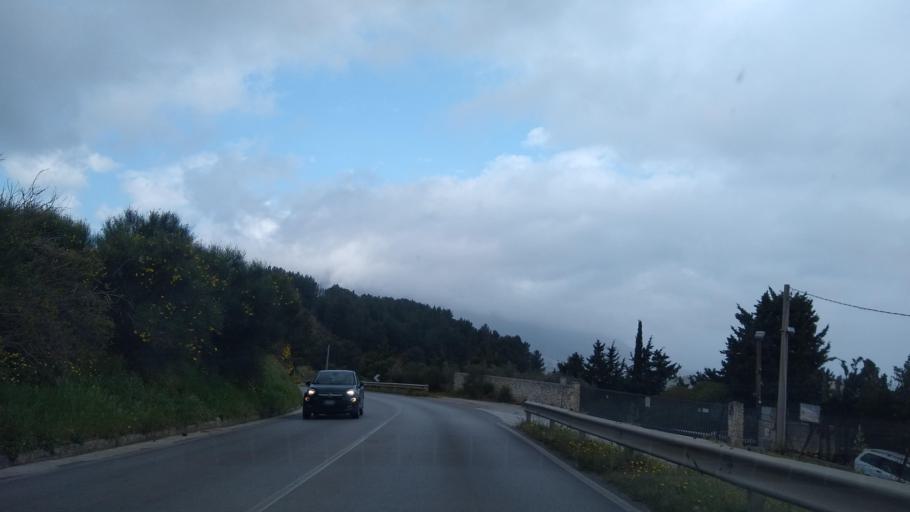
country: IT
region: Sicily
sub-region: Trapani
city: Alcamo
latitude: 37.9765
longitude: 12.9413
